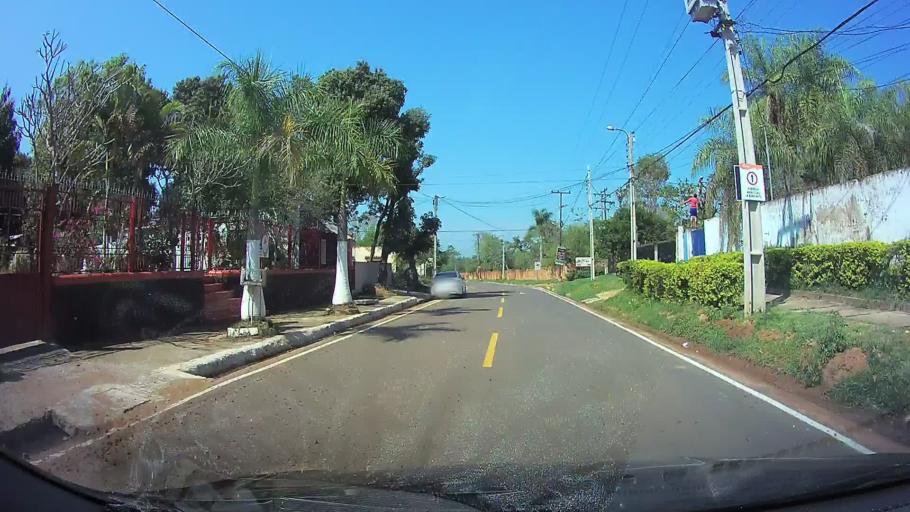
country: PY
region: Central
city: Limpio
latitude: -25.2377
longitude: -57.5014
